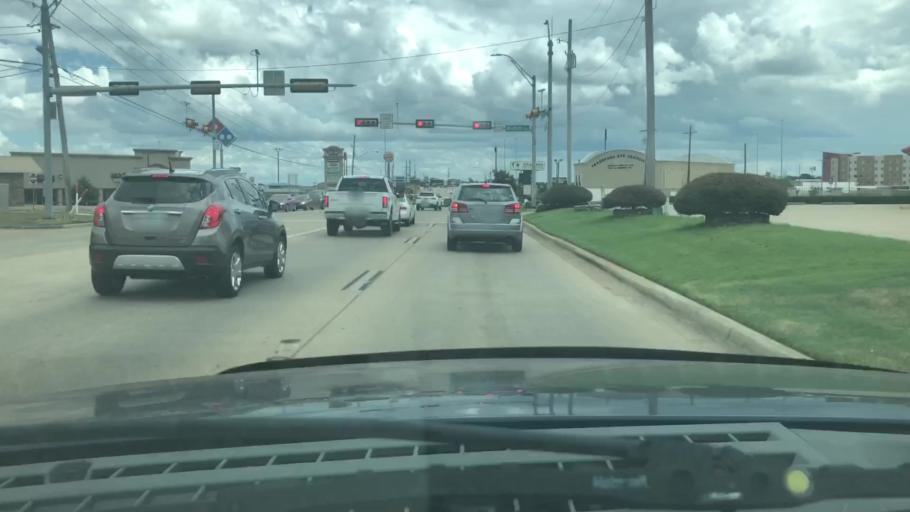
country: US
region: Texas
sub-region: Bowie County
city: Wake Village
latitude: 33.4608
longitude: -94.0912
